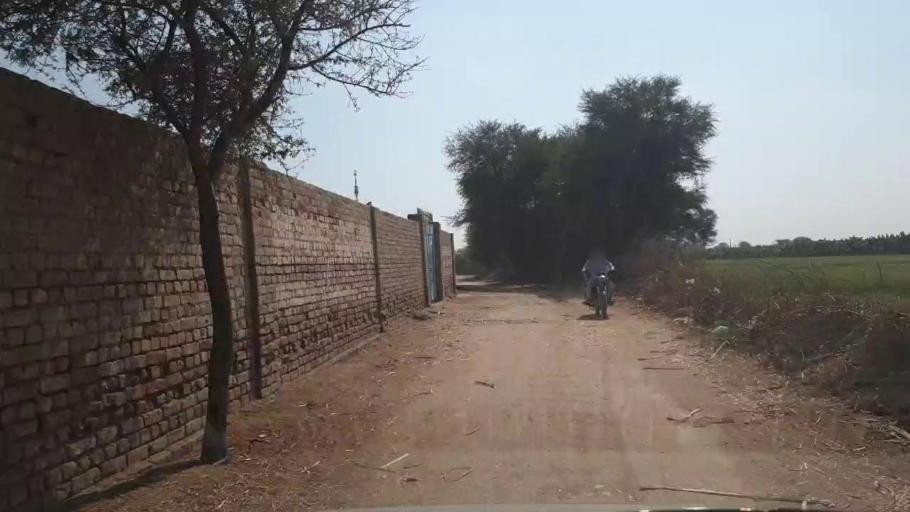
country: PK
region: Sindh
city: Chambar
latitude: 25.3522
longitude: 68.8232
